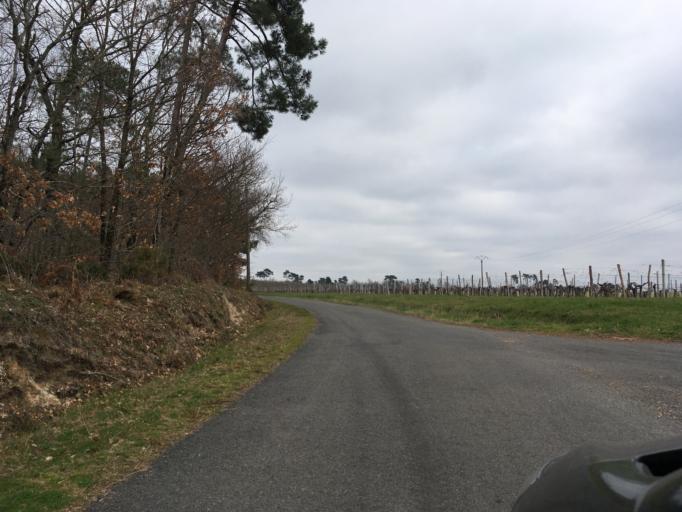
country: FR
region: Aquitaine
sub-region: Departement de la Gironde
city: Saint-Ciers-sur-Gironde
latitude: 45.3183
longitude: -0.6017
